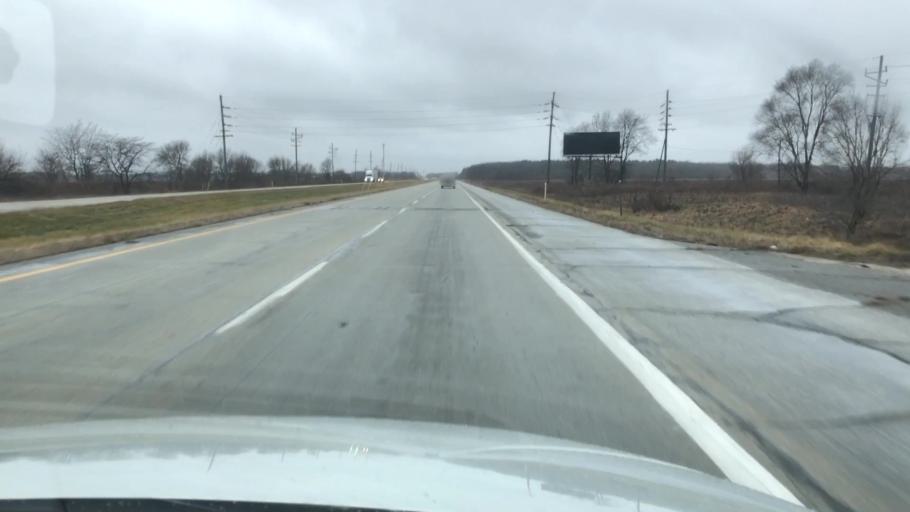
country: US
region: Indiana
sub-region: Starke County
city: Koontz Lake
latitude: 41.3744
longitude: -86.5260
